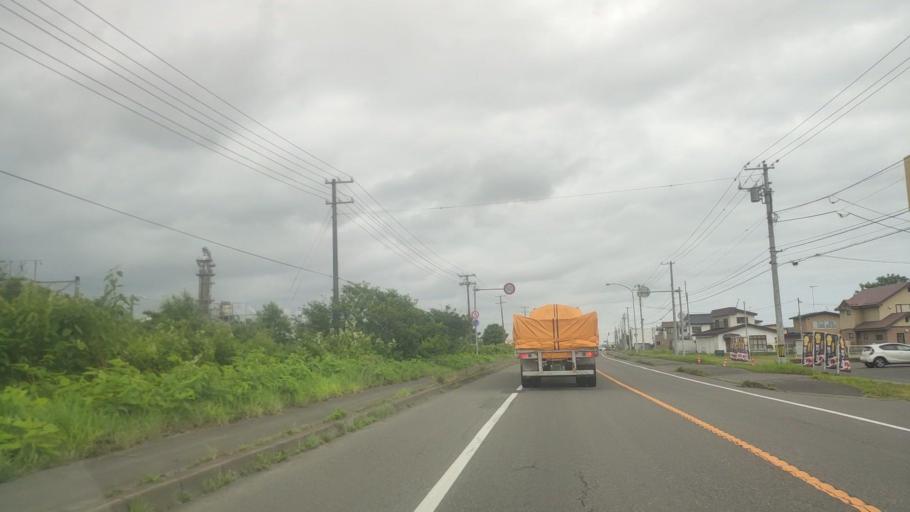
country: JP
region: Hokkaido
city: Shiraoi
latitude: 42.5080
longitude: 141.2853
